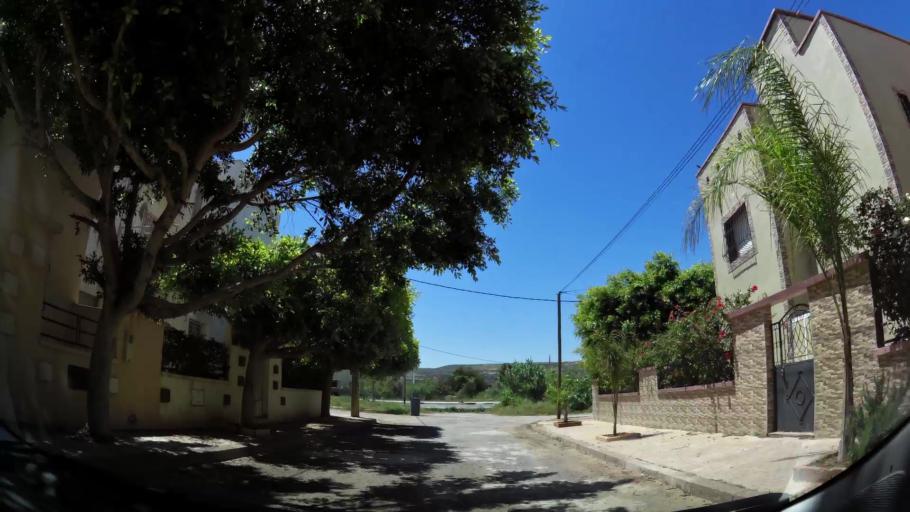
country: MA
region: Oriental
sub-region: Berkane-Taourirt
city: Madagh
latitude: 35.0823
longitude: -2.2427
